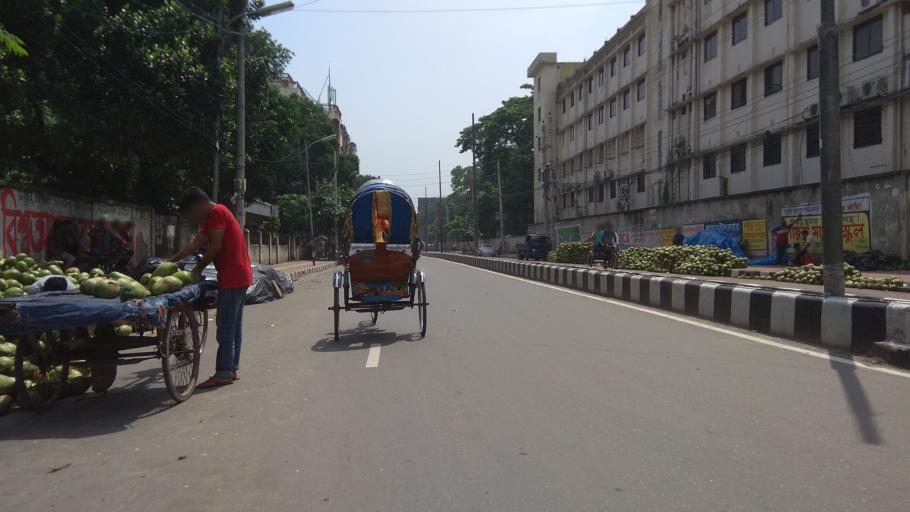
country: BD
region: Dhaka
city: Azimpur
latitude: 23.8044
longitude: 90.3601
